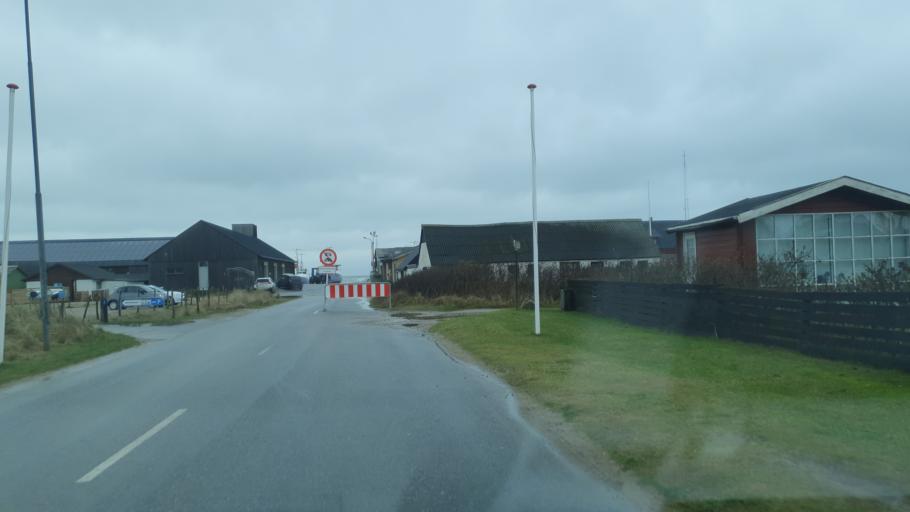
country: DK
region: North Denmark
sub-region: Jammerbugt Kommune
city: Fjerritslev
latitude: 57.1386
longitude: 9.1260
